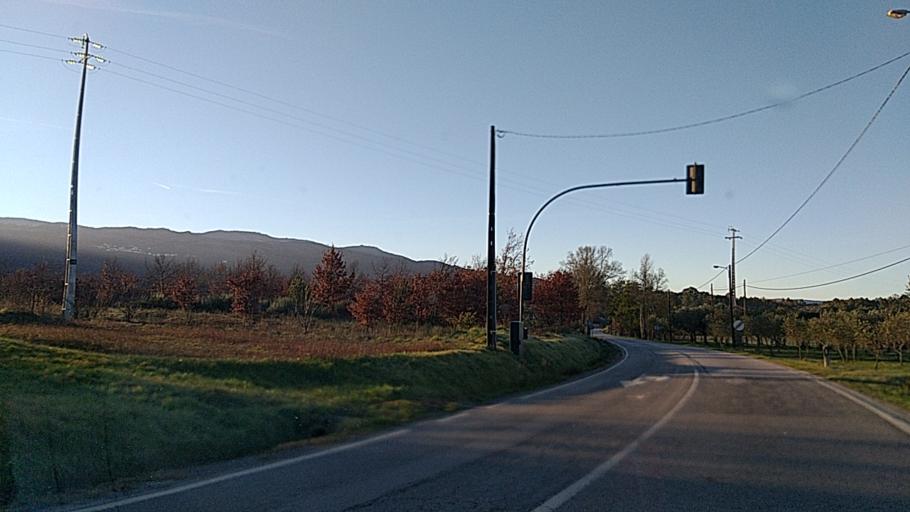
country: PT
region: Guarda
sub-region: Seia
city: Seia
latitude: 40.4487
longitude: -7.7103
